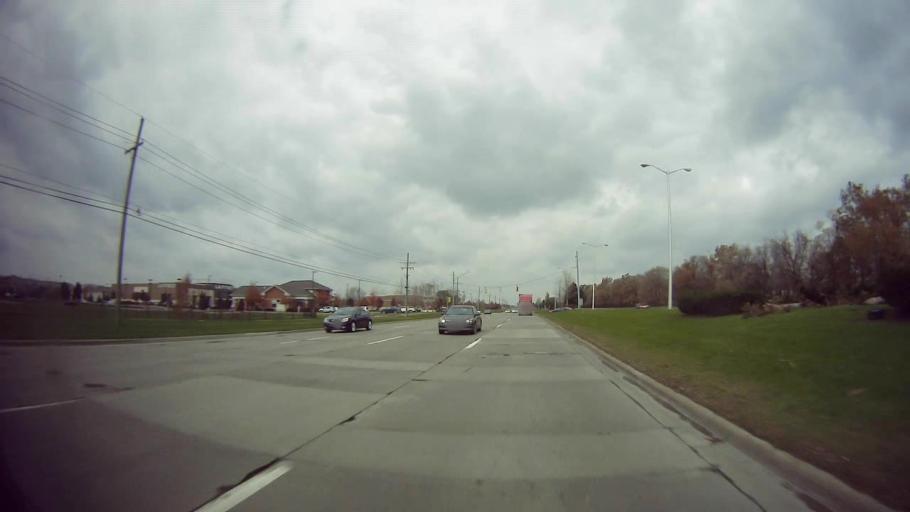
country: US
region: Michigan
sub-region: Macomb County
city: Center Line
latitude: 42.5124
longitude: -83.0469
